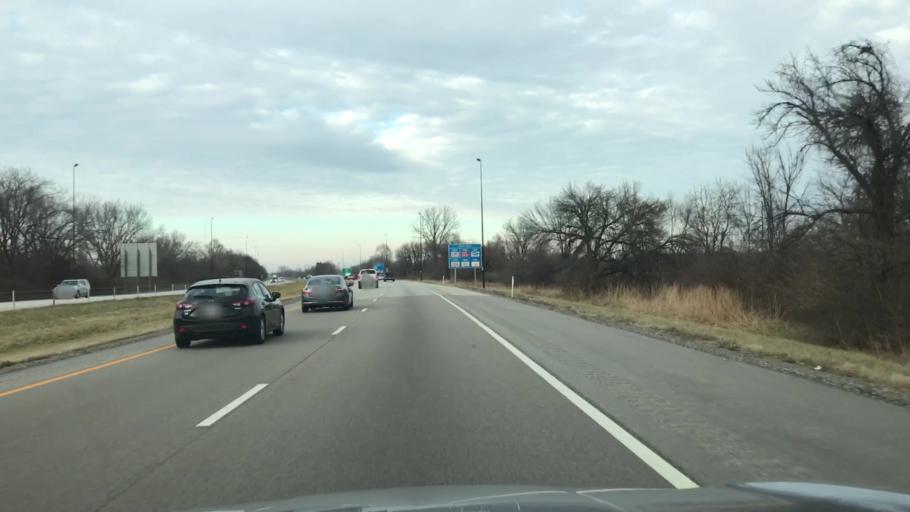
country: US
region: Illinois
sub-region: Sangamon County
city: Grandview
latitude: 39.8082
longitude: -89.5933
